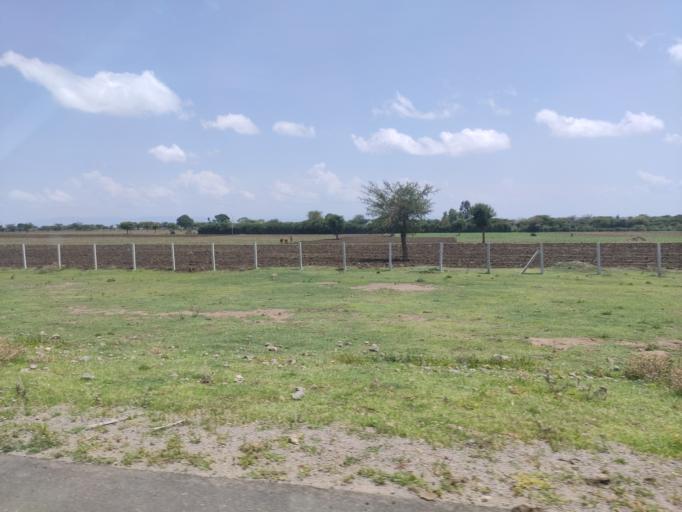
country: ET
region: Oromiya
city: Ziway
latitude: 8.2505
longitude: 38.8886
